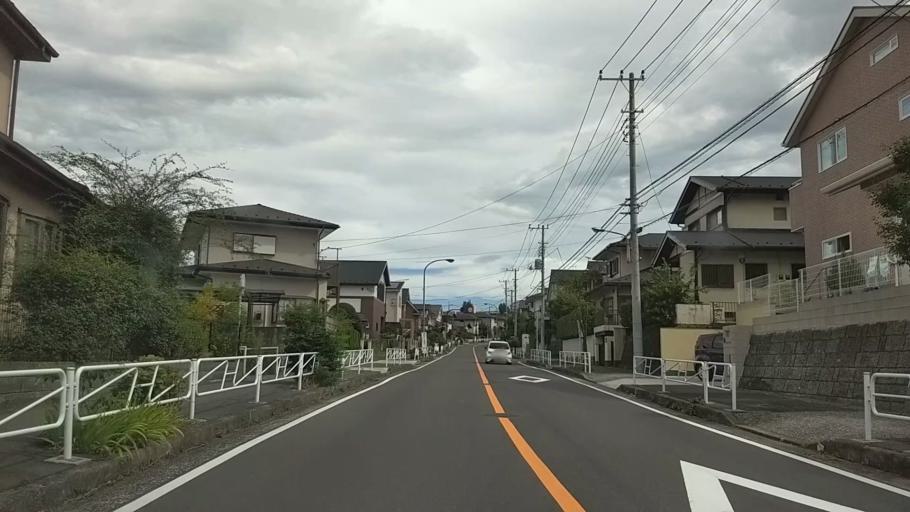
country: JP
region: Tokyo
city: Hachioji
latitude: 35.6346
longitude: 139.3433
